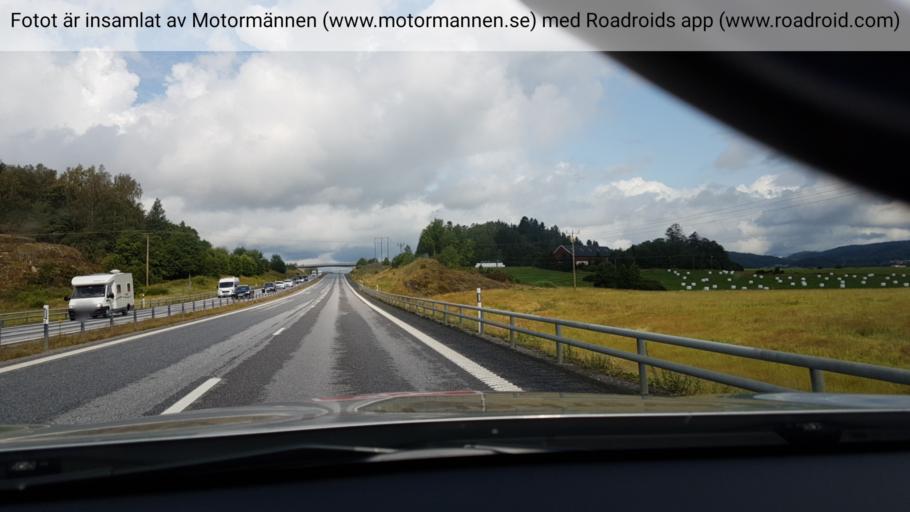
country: SE
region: Vaestra Goetaland
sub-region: Munkedals Kommun
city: Munkedal
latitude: 58.5027
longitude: 11.5656
